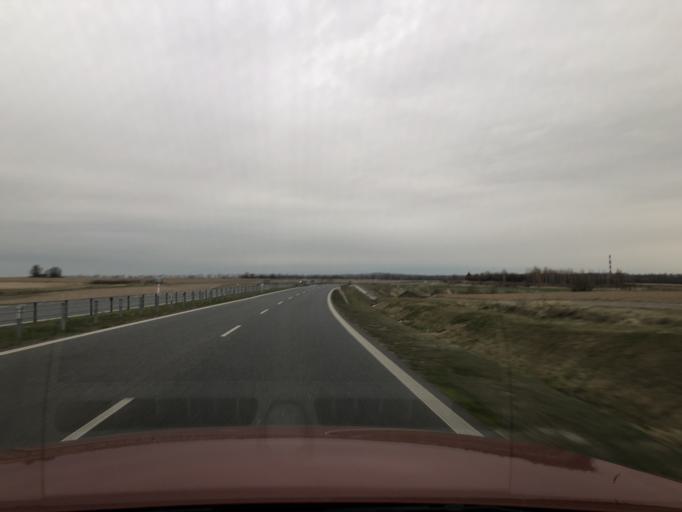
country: PL
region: Lower Silesian Voivodeship
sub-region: Powiat swidnicki
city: Swidnica
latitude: 50.8514
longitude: 16.4380
